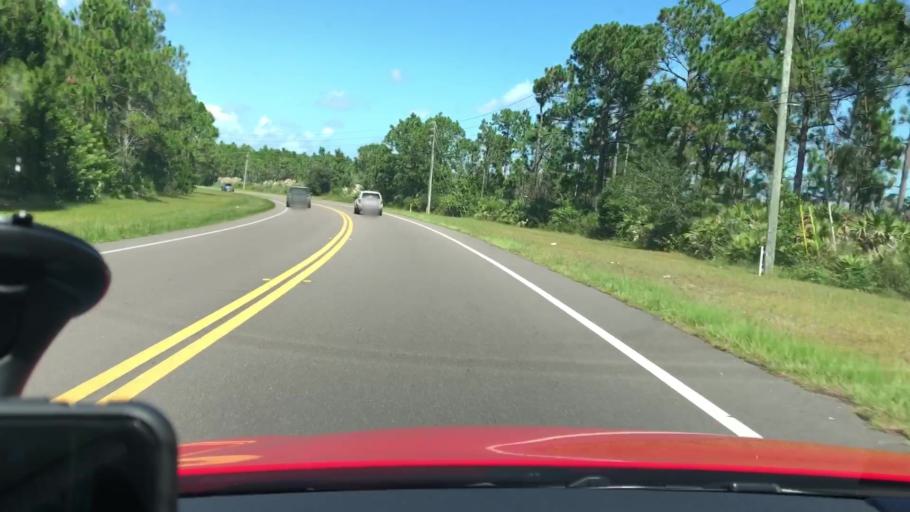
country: US
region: Florida
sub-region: Volusia County
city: Ormond Beach
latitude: 29.2551
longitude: -81.0990
